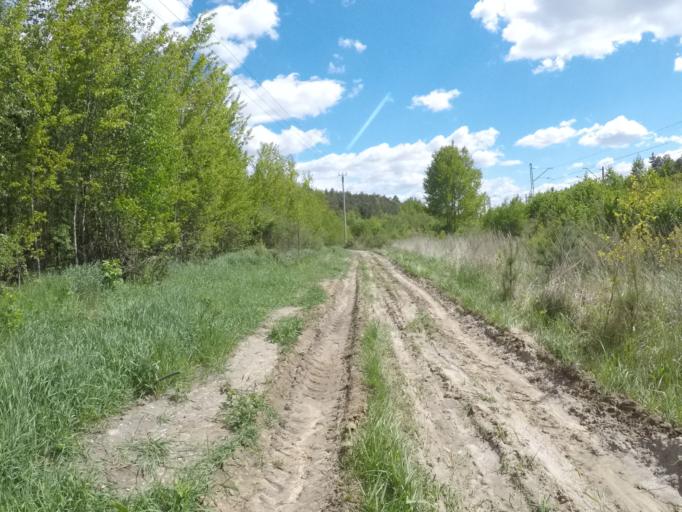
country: PL
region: Swietokrzyskie
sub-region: Powiat kielecki
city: Kostomloty Pierwsze
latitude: 50.9186
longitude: 20.6219
